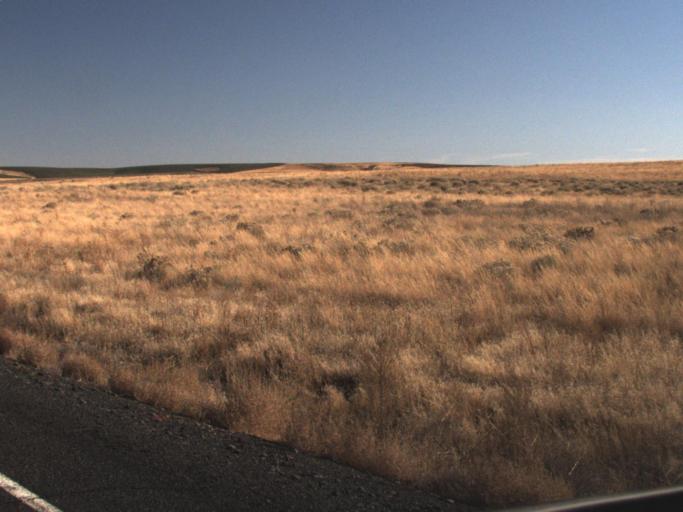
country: US
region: Washington
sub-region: Franklin County
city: Connell
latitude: 46.7107
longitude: -118.5359
